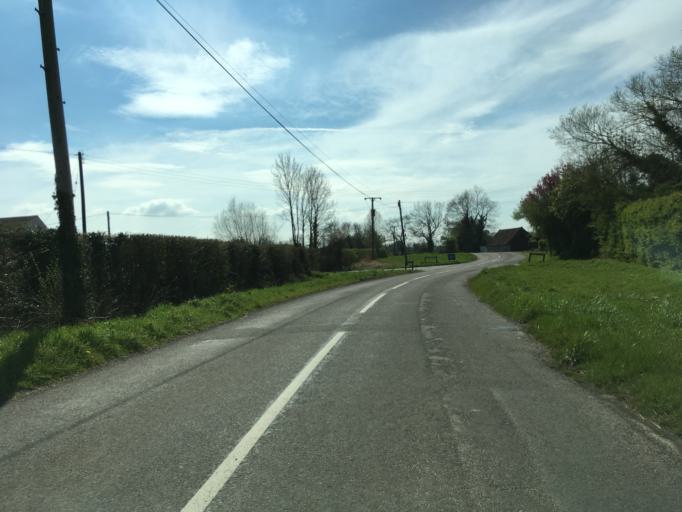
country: GB
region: England
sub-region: South Gloucestershire
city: Severn Beach
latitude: 51.5626
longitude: -2.6211
